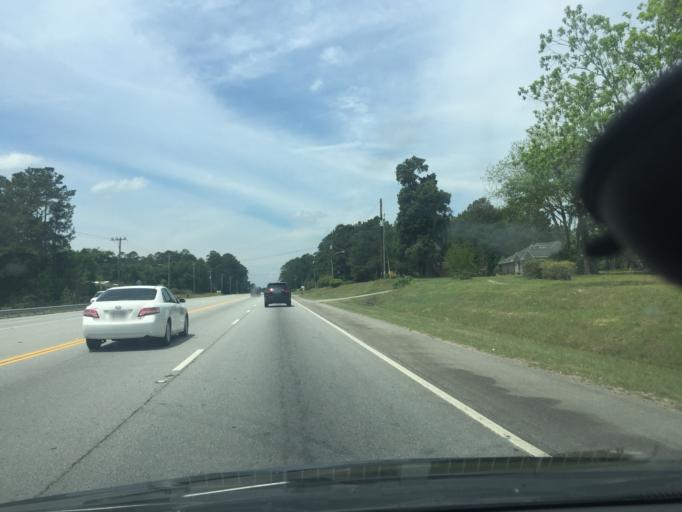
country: US
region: Georgia
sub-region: Chatham County
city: Bloomingdale
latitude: 32.1388
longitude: -81.3188
